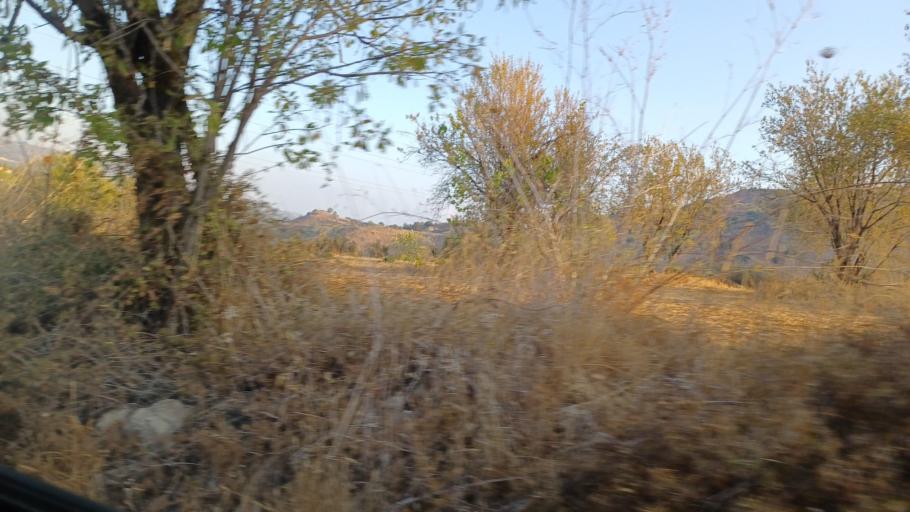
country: CY
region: Pafos
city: Tala
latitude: 34.9173
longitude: 32.4905
